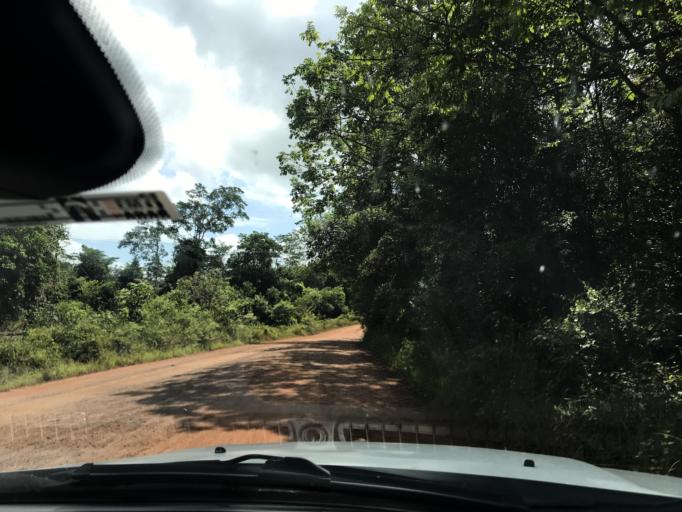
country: BR
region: Bahia
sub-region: Entre Rios
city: Entre Rios
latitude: -12.1673
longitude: -38.0706
